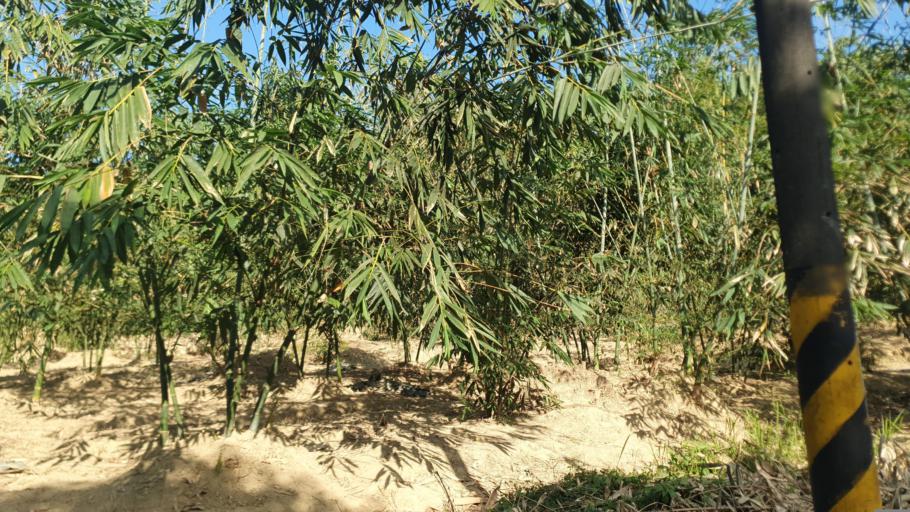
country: TW
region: Taiwan
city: Yujing
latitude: 23.0150
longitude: 120.3850
